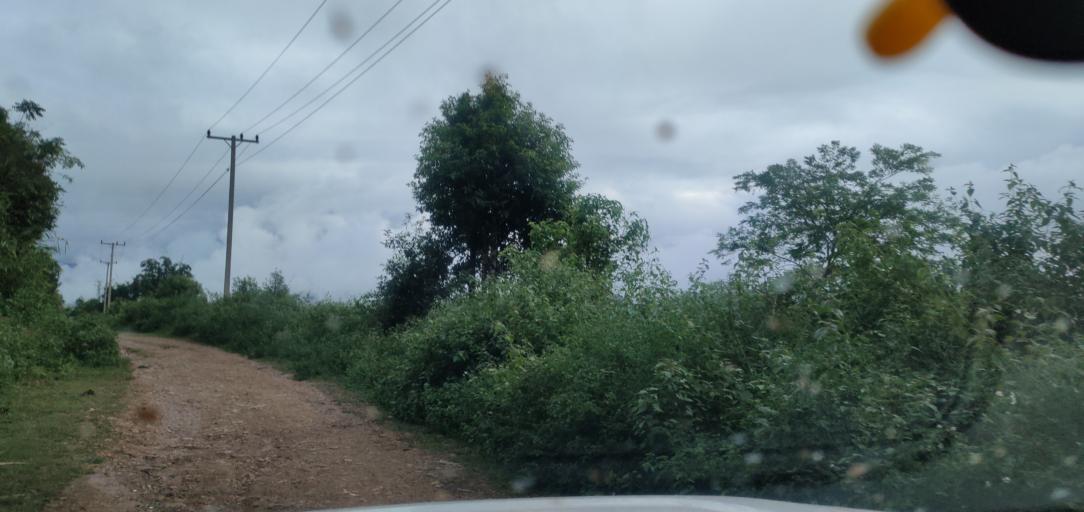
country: LA
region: Phongsali
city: Phongsali
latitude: 21.4453
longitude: 102.2932
